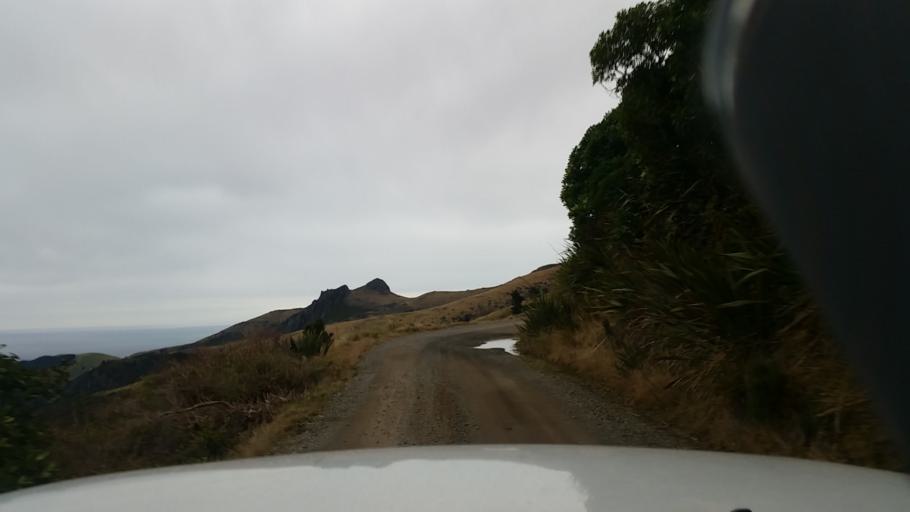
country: NZ
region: Canterbury
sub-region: Christchurch City
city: Christchurch
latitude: -43.8090
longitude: 172.8530
